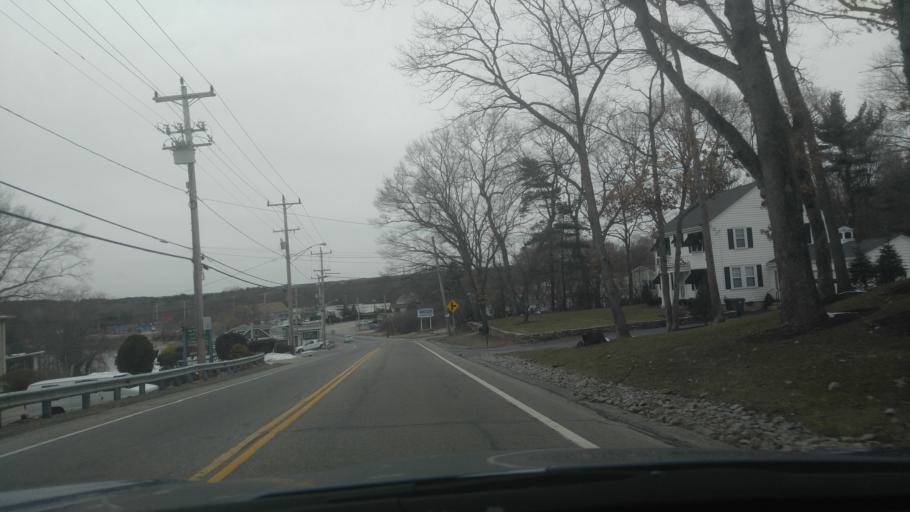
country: US
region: Rhode Island
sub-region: Kent County
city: West Warwick
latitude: 41.6842
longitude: -71.5456
